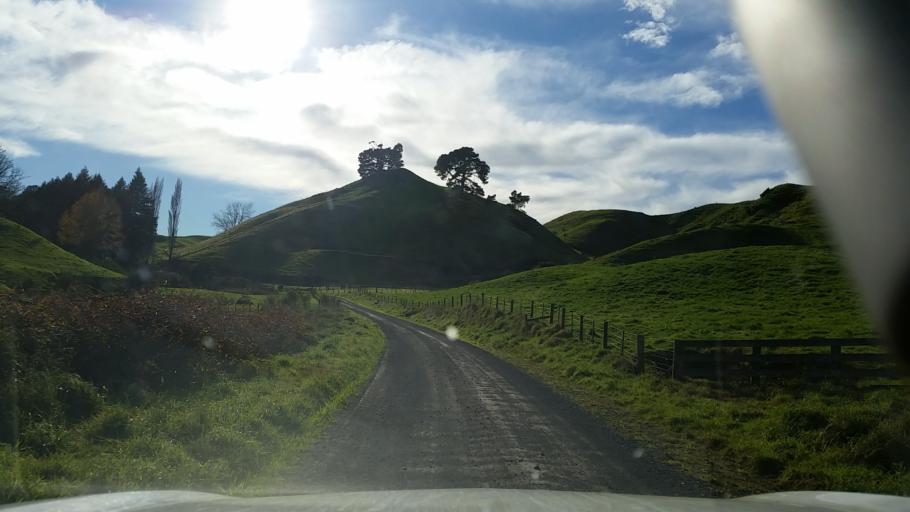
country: NZ
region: Waikato
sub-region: South Waikato District
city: Tokoroa
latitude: -38.3701
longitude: 176.0878
